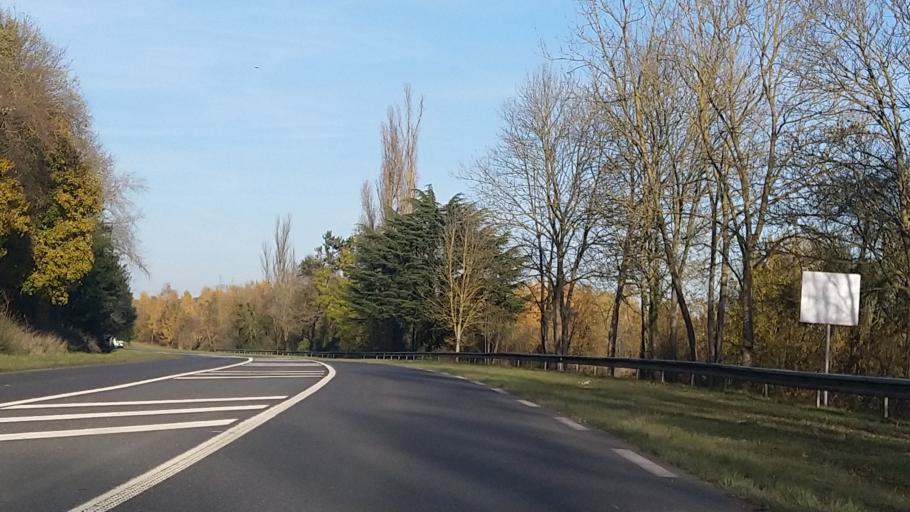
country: FR
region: Ile-de-France
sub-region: Departement du Val-d'Oise
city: Ecouen
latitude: 49.0471
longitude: 2.4013
